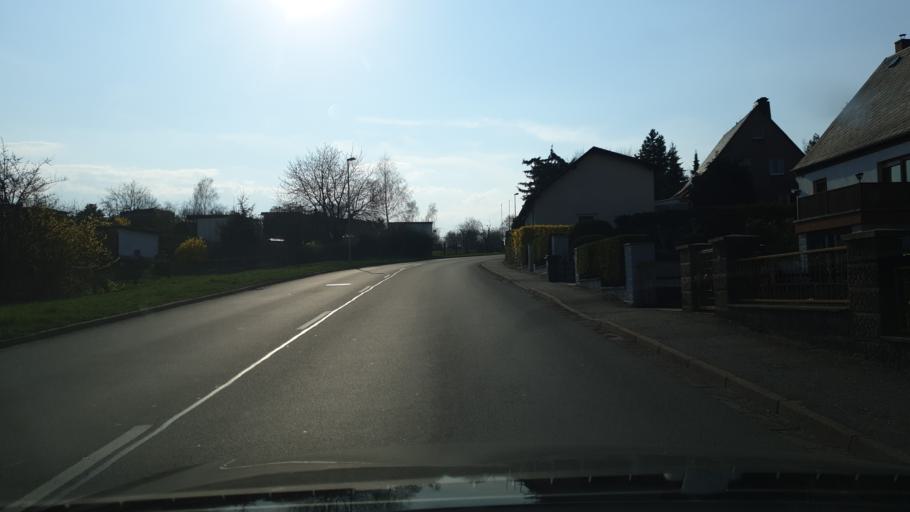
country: DE
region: Saxony
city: Mittweida
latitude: 50.9805
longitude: 12.9731
